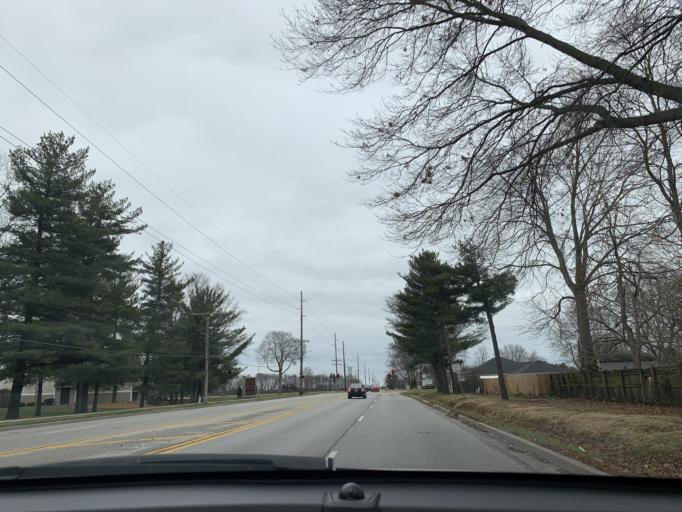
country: US
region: Illinois
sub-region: Sangamon County
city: Jerome
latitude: 39.7582
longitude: -89.6868
